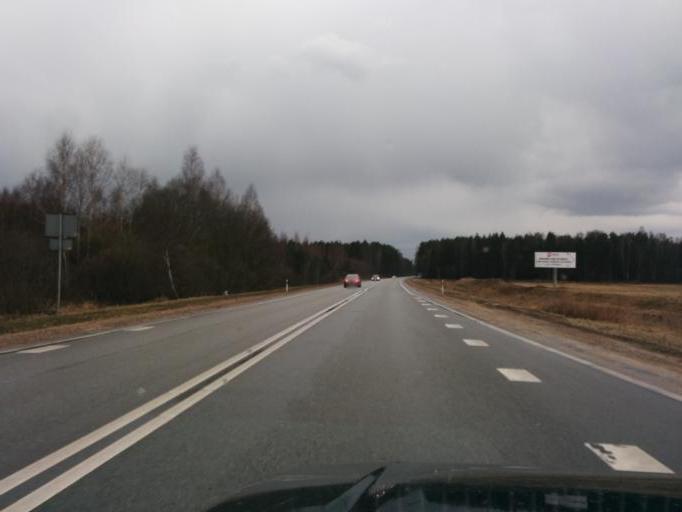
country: LV
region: Marupe
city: Marupe
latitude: 56.8399
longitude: 24.0261
